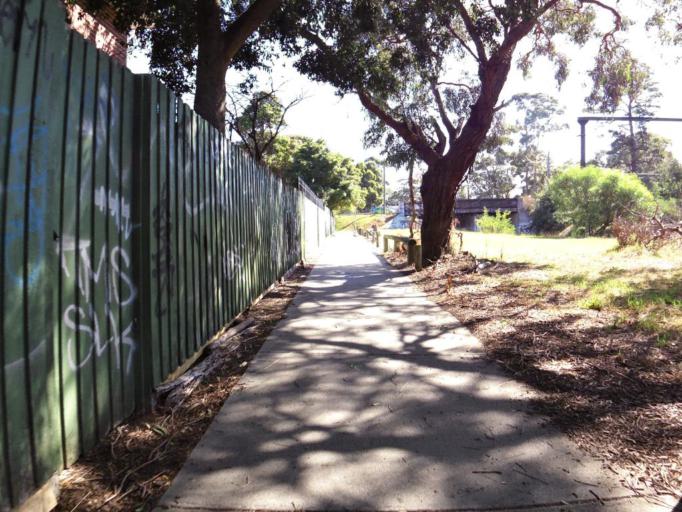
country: AU
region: Victoria
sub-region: Monash
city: Ashwood
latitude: -37.8754
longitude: 145.1301
